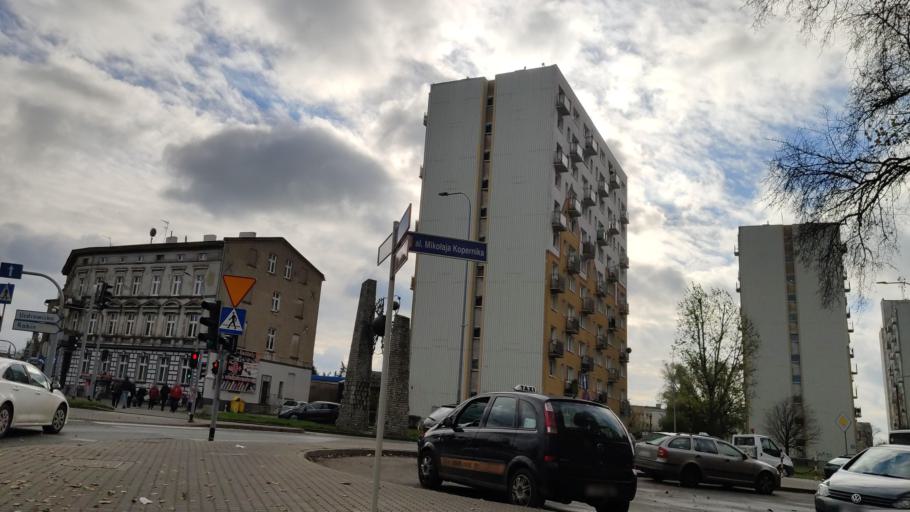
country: PL
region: Kujawsko-Pomorskie
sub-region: Powiat inowroclawski
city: Inowroclaw
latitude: 52.8021
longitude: 18.2512
